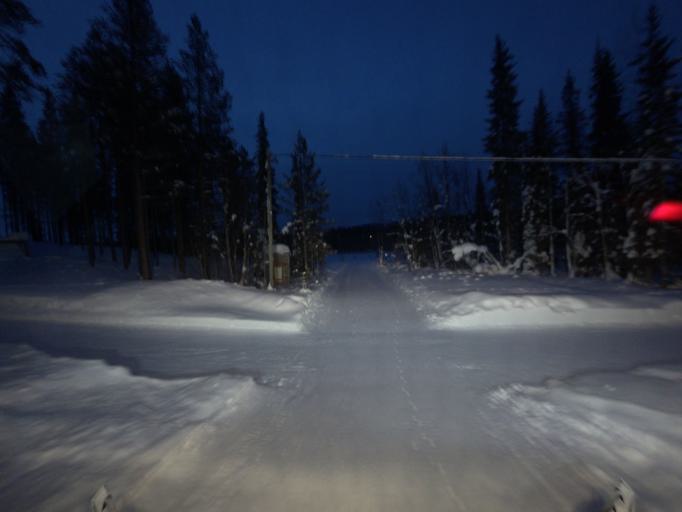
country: FI
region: Lapland
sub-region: Tunturi-Lappi
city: Kolari
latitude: 67.6042
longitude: 24.1329
